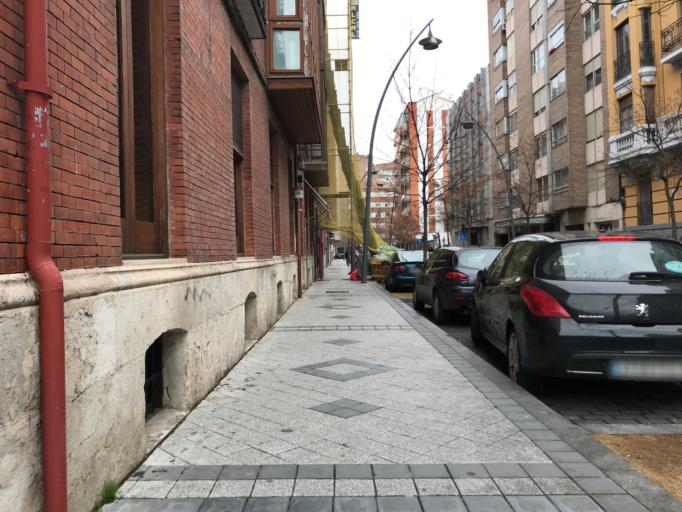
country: ES
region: Castille and Leon
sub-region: Provincia de Valladolid
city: Valladolid
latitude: 41.6448
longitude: -4.7263
